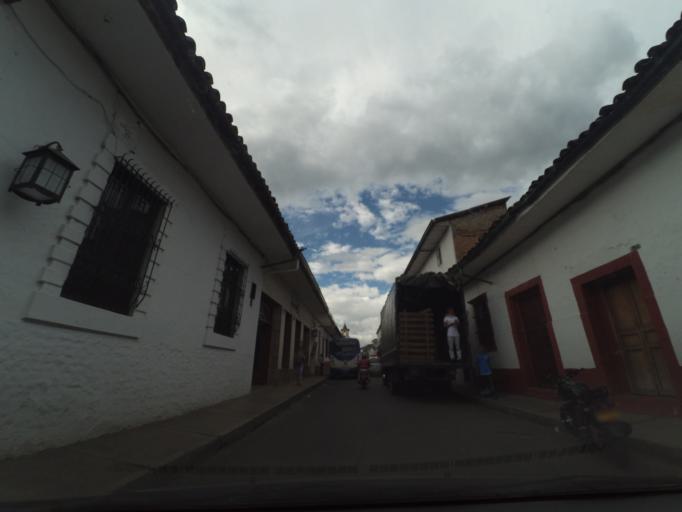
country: CO
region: Cauca
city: Popayan
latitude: 2.4411
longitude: -76.6080
